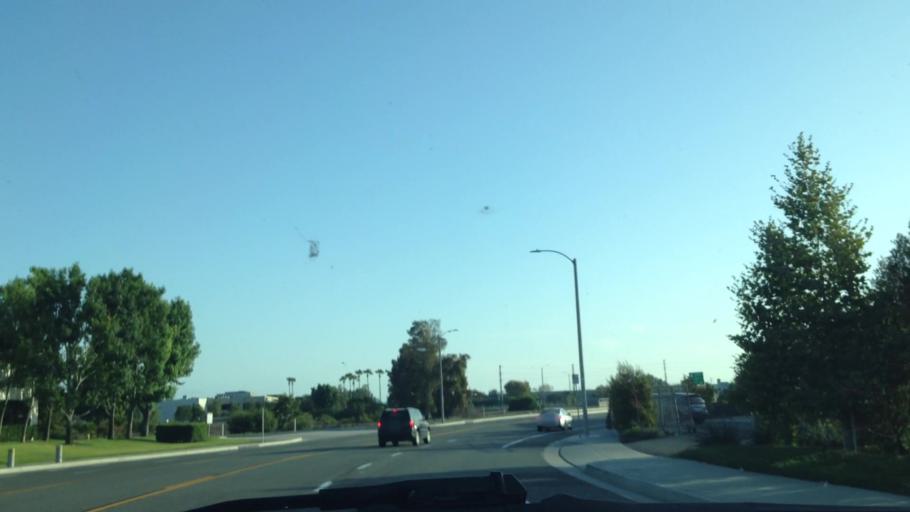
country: US
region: California
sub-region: Orange County
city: Tustin
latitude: 33.7231
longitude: -117.8333
